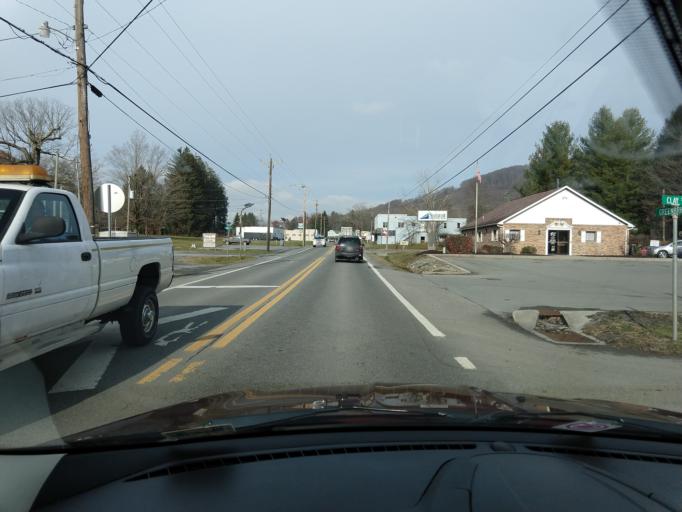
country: US
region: West Virginia
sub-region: Greenbrier County
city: Rainelle
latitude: 37.9613
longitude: -80.6857
